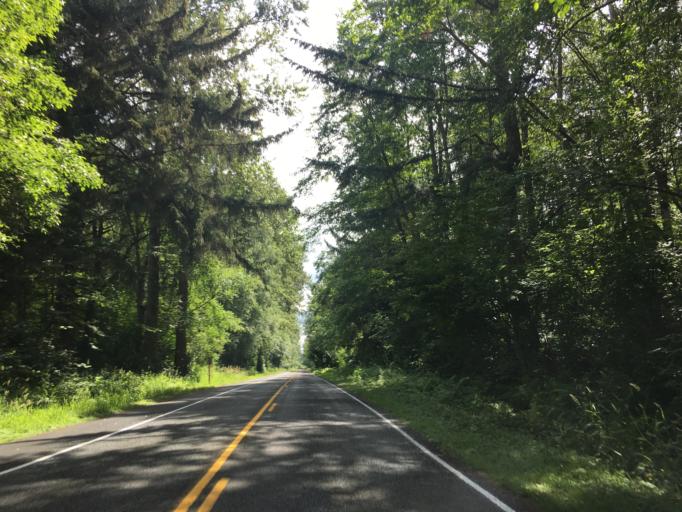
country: US
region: Washington
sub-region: Whatcom County
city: Birch Bay
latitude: 48.9033
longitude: -122.7592
